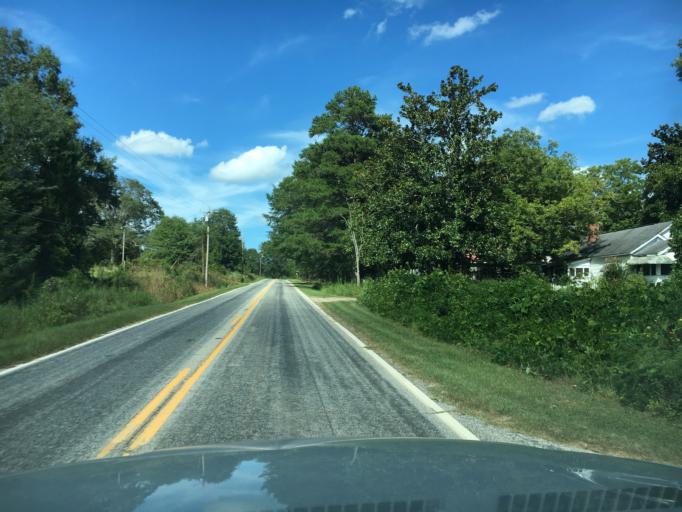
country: US
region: South Carolina
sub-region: Greenwood County
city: Ware Shoals
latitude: 34.4195
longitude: -82.2847
